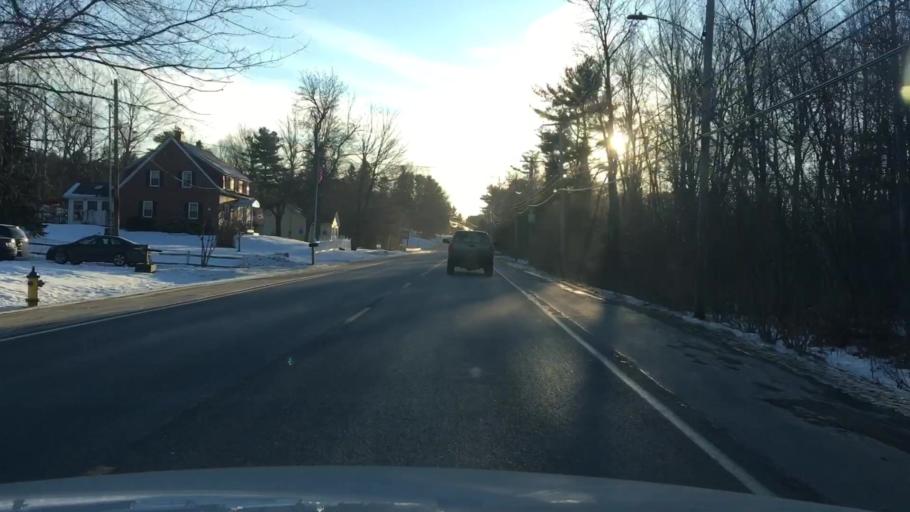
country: US
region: Maine
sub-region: Penobscot County
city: Brewer
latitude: 44.8092
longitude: -68.7377
